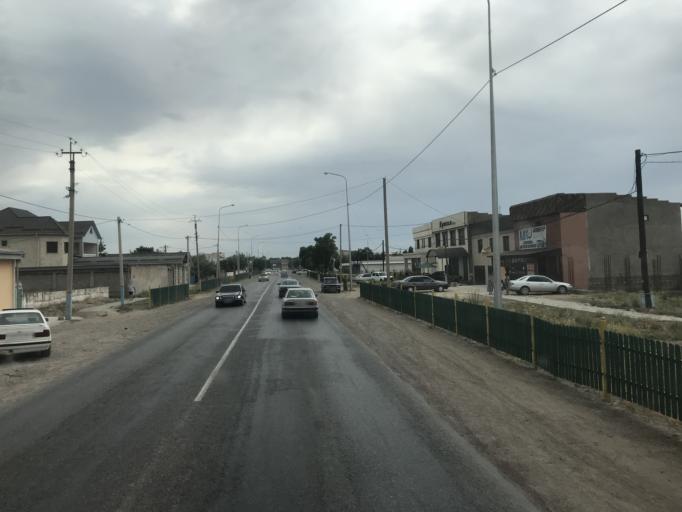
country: KZ
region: Ongtustik Qazaqstan
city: Saryaghash
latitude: 41.3477
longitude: 68.9606
